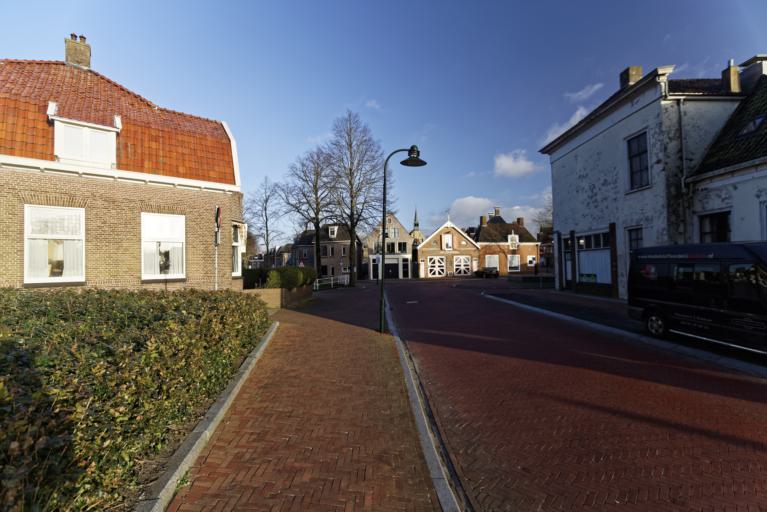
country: NL
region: Friesland
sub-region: Gemeente Dongeradeel
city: Dokkum
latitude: 53.3269
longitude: 5.9951
